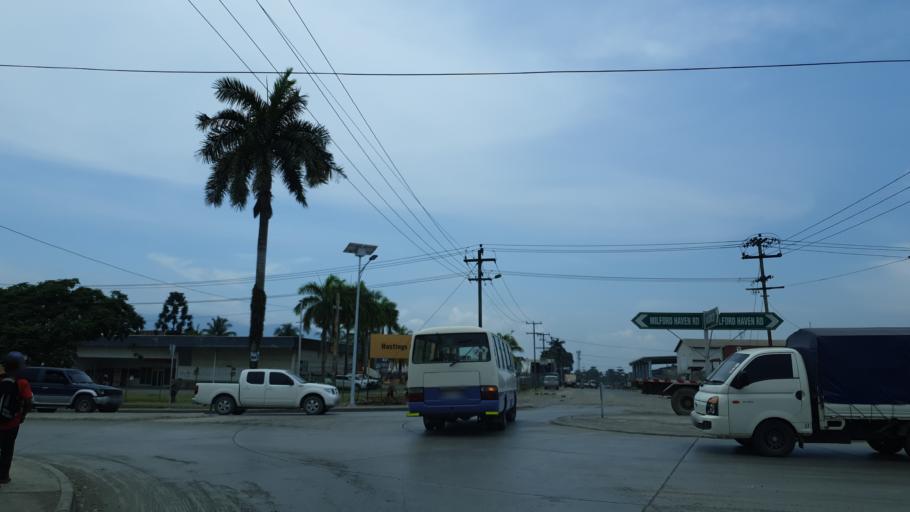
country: PG
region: Morobe
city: Lae
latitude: -6.7309
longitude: 146.9880
